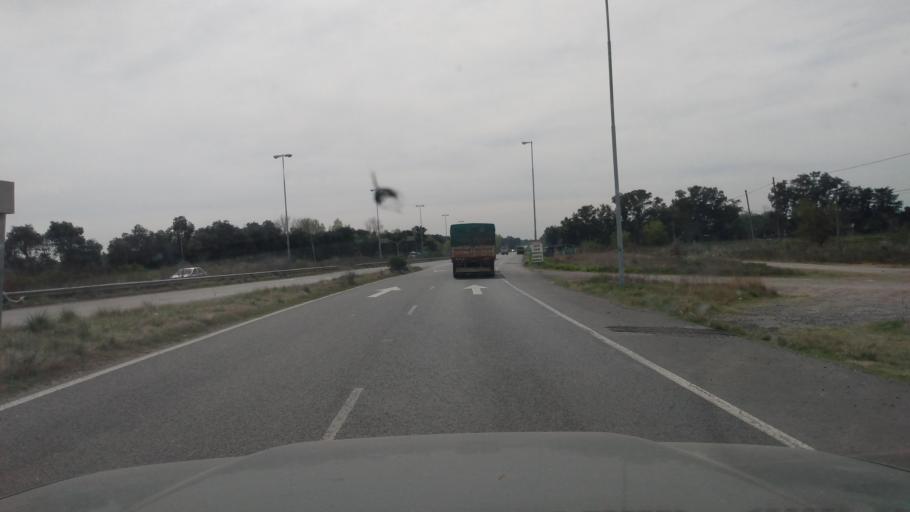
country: AR
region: Buenos Aires
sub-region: Partido de Lujan
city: Lujan
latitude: -34.4702
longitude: -59.0679
